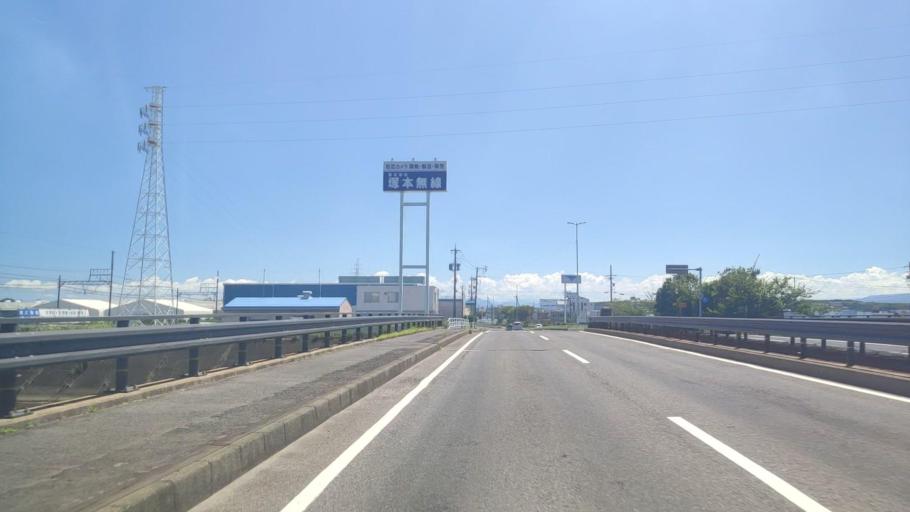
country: JP
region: Mie
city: Kawage
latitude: 34.8081
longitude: 136.5639
